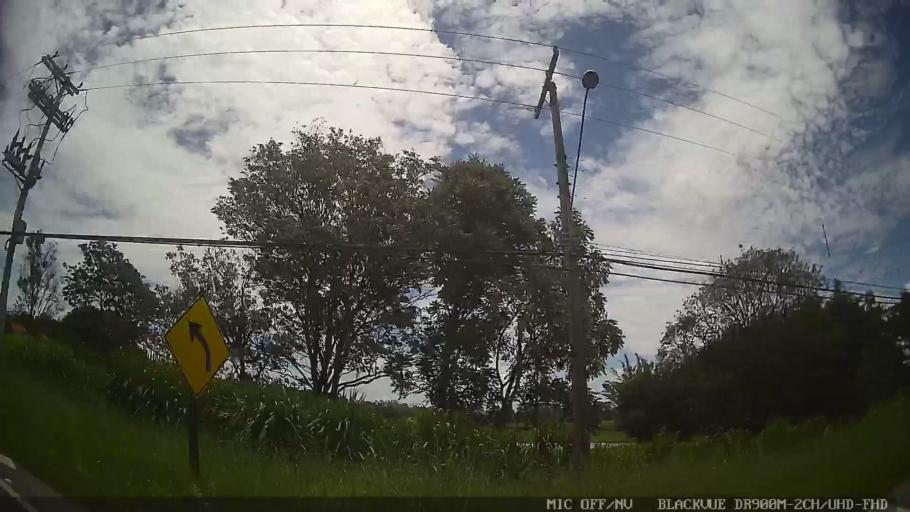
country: BR
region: Sao Paulo
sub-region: Conchas
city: Conchas
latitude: -23.0661
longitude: -47.9734
